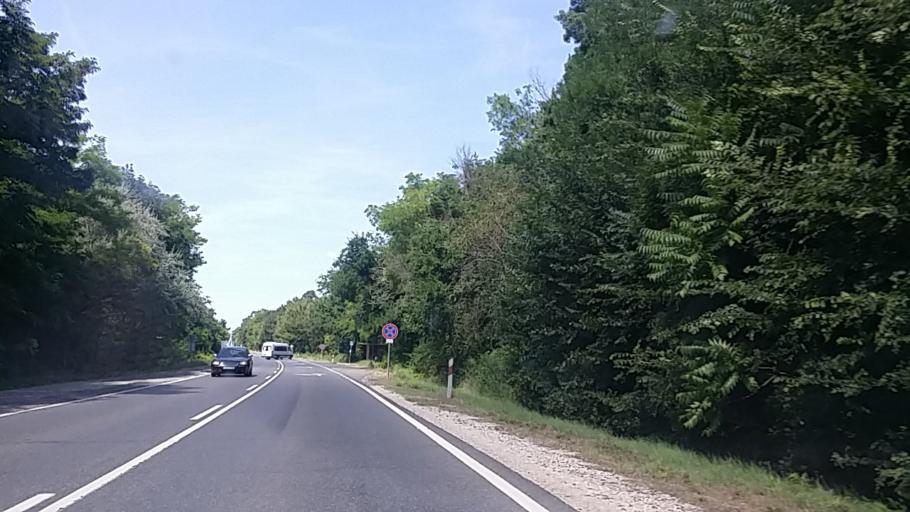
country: HU
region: Fejer
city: Deg
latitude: 46.8668
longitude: 18.4142
